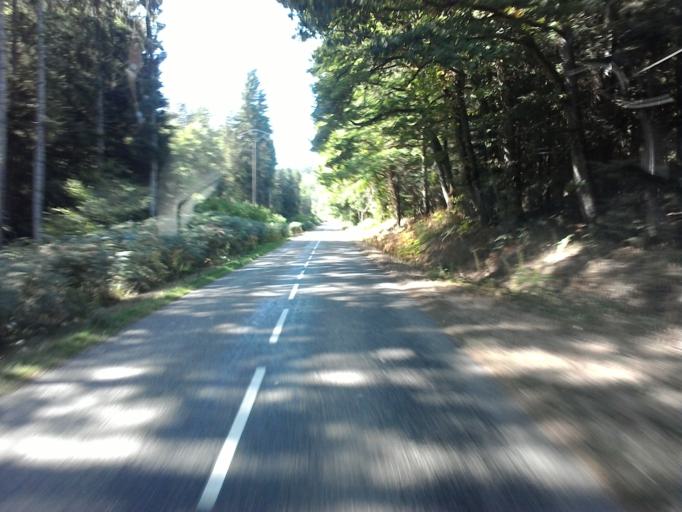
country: FR
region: Bourgogne
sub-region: Departement de la Cote-d'Or
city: Saulieu
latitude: 47.2814
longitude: 4.0728
